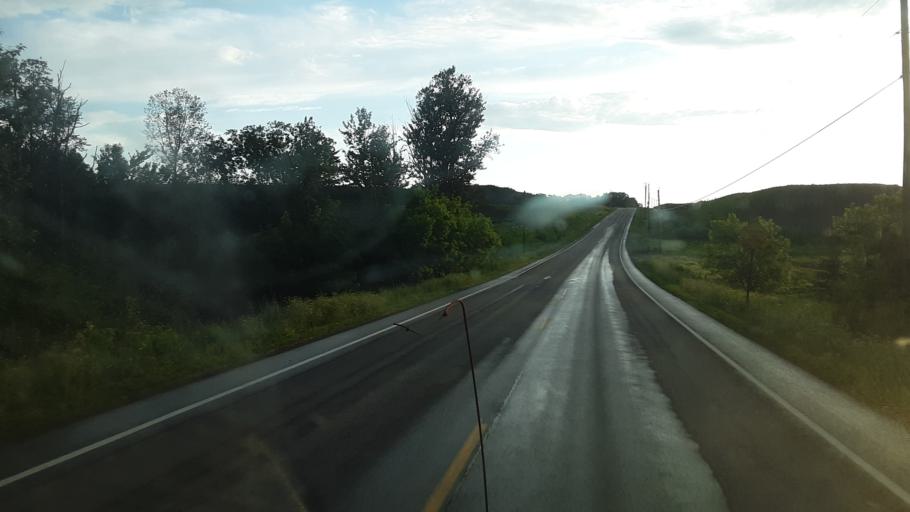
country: US
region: Maine
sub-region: Aroostook County
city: Presque Isle
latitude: 46.6749
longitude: -67.9679
